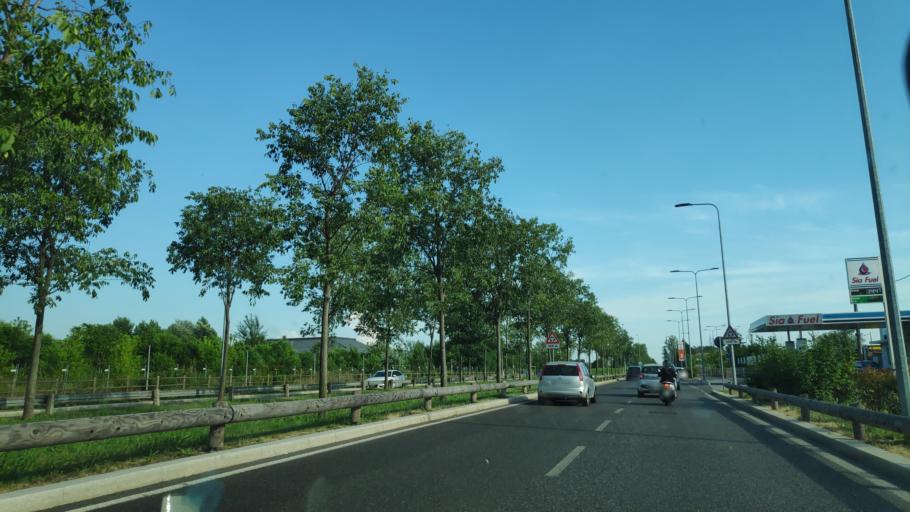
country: IT
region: Lombardy
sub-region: Citta metropolitana di Milano
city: Noverasco-Sporting Mirasole
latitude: 45.4176
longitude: 9.2053
